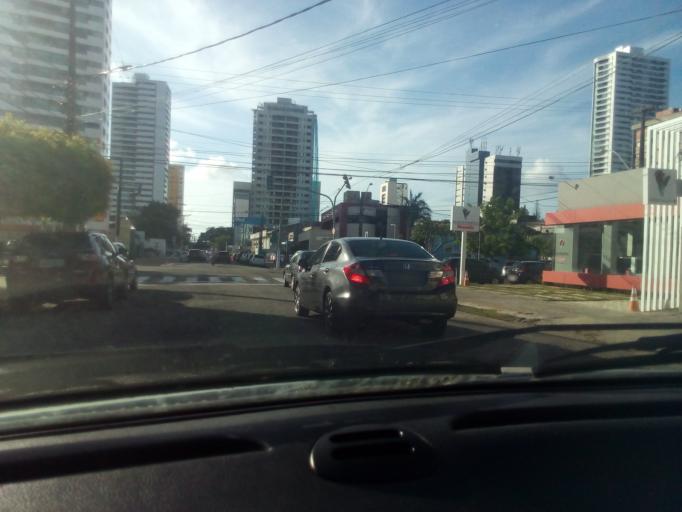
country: BR
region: Rio Grande do Norte
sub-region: Natal
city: Natal
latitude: -5.7915
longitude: -35.2007
